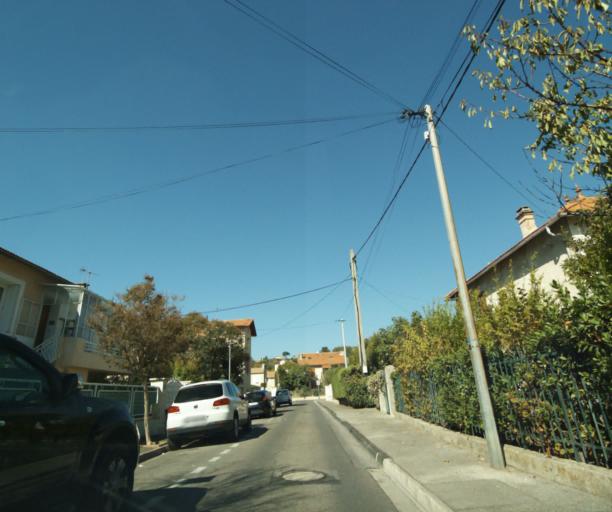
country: FR
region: Provence-Alpes-Cote d'Azur
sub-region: Departement des Bouches-du-Rhone
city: Plan-de-Cuques
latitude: 43.3468
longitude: 5.4598
